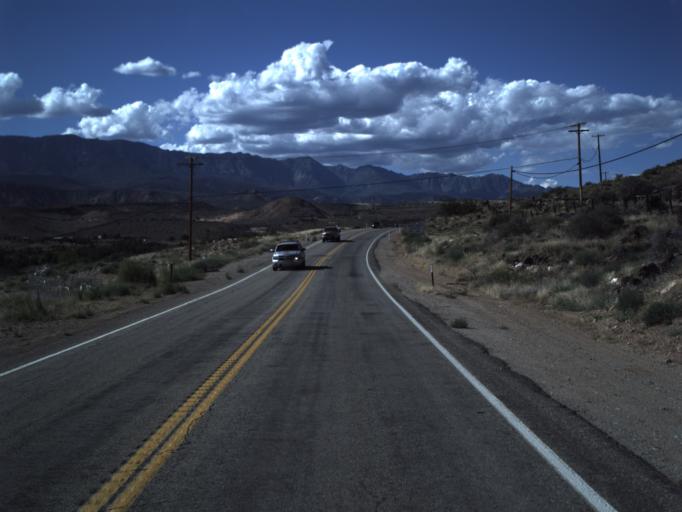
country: US
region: Utah
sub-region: Washington County
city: Toquerville
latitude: 37.2438
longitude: -113.2830
